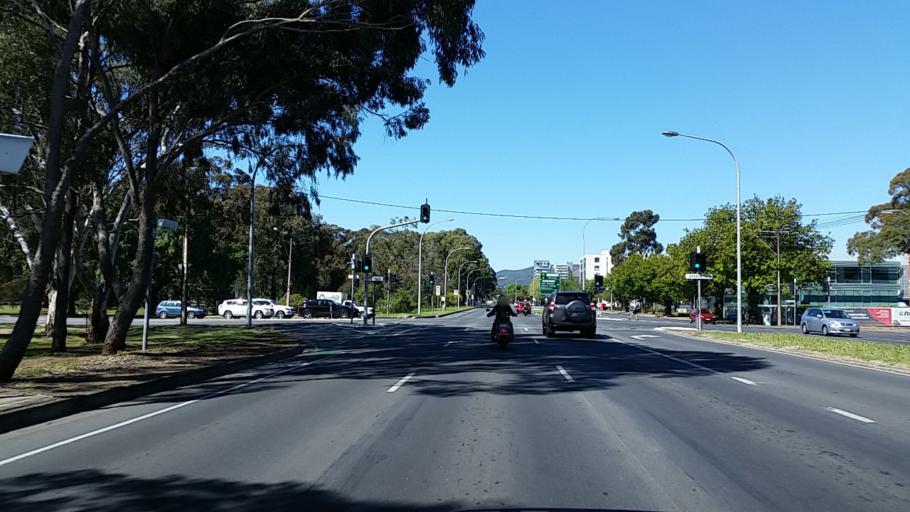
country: AU
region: South Australia
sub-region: Unley
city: Unley
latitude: -34.9406
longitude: 138.6121
